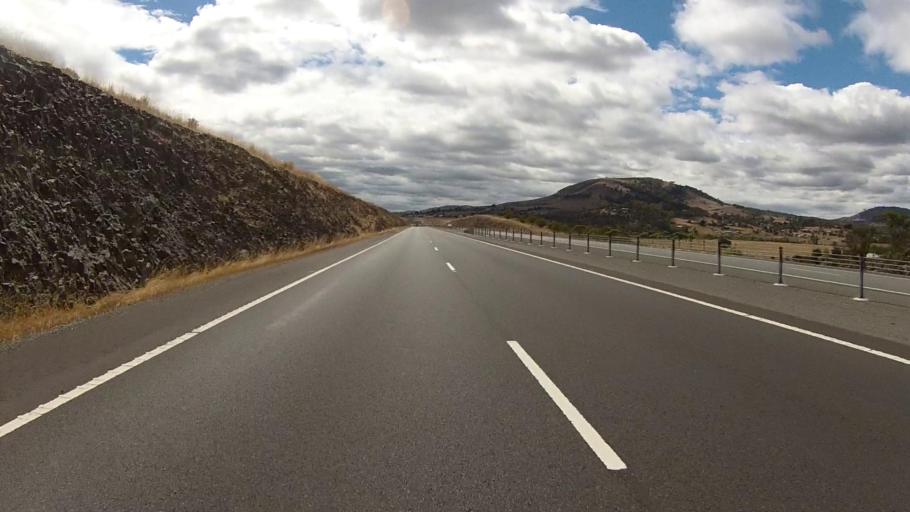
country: AU
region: Tasmania
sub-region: Brighton
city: Bridgewater
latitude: -42.7080
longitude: 147.2535
